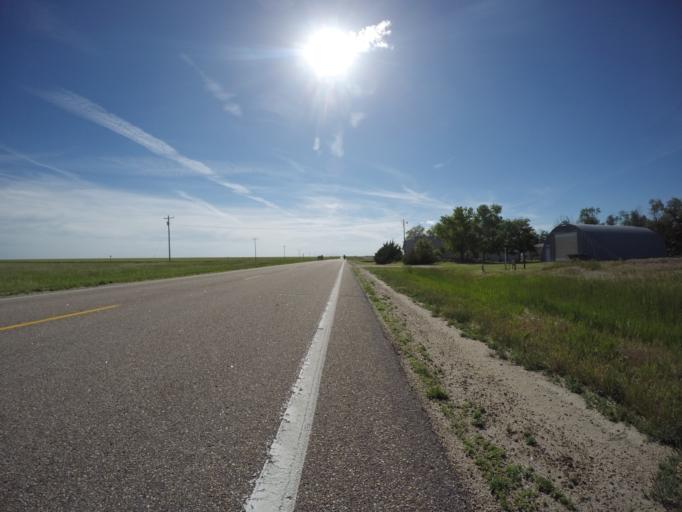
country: US
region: Kansas
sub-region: Cheyenne County
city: Saint Francis
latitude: 39.7566
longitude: -101.9924
